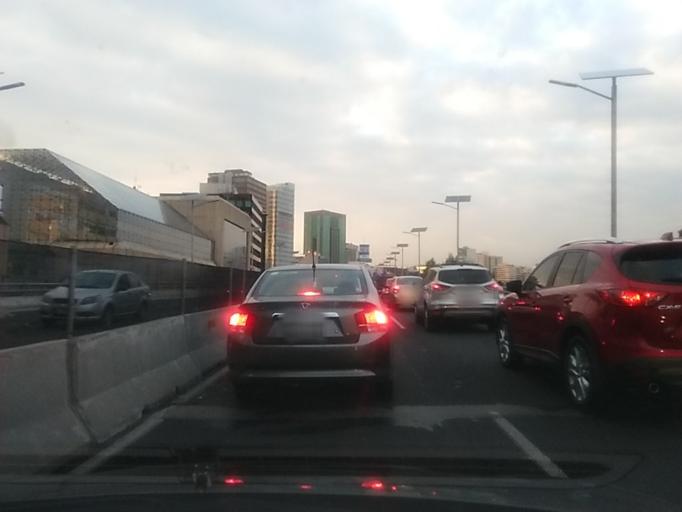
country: MX
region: Mexico City
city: Miguel Hidalgo
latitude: 19.4301
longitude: -99.2058
